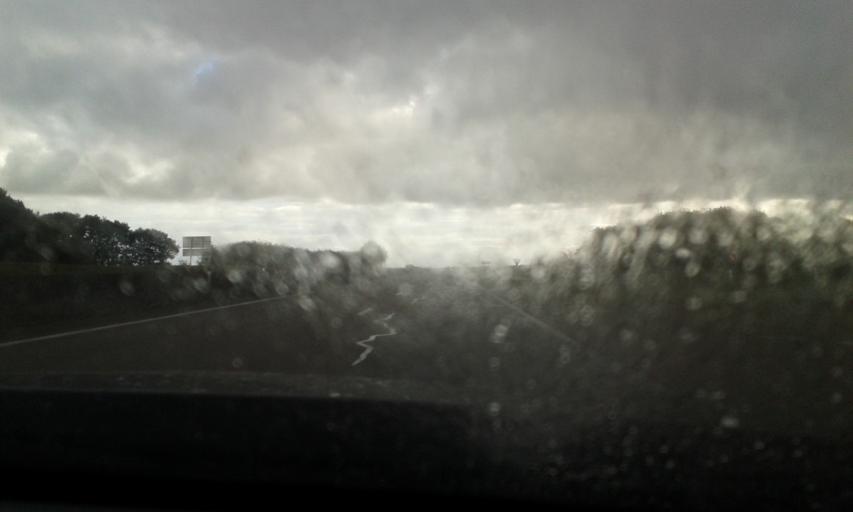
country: FR
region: Haute-Normandie
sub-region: Departement de l'Eure
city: La Madeleine-de-Nonancourt
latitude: 48.8532
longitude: 1.1794
